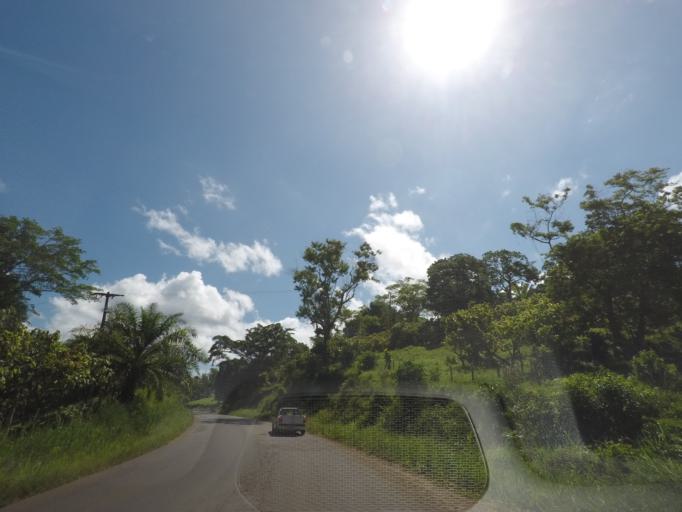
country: BR
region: Bahia
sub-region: Taperoa
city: Taperoa
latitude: -13.5546
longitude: -39.1041
